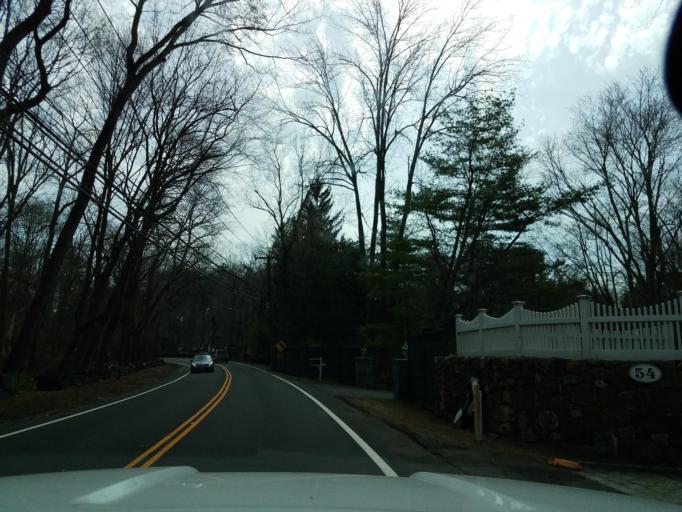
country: US
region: Connecticut
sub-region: Fairfield County
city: Greenwich
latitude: 41.0312
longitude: -73.6415
